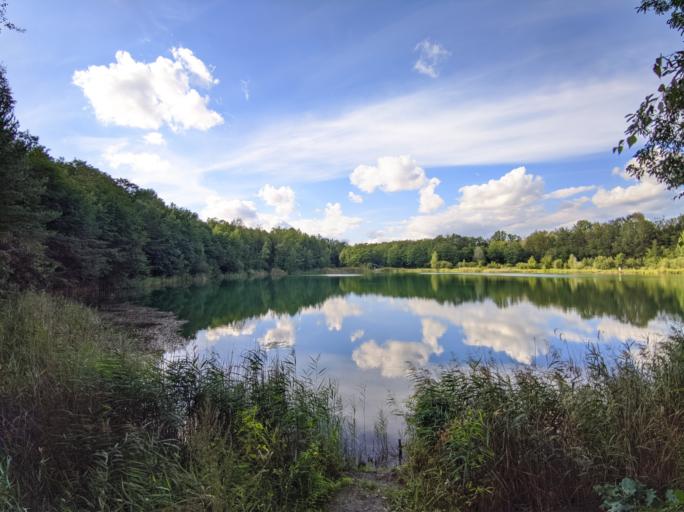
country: PL
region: Lubusz
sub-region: Powiat zarski
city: Jasien
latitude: 51.7548
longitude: 15.0279
